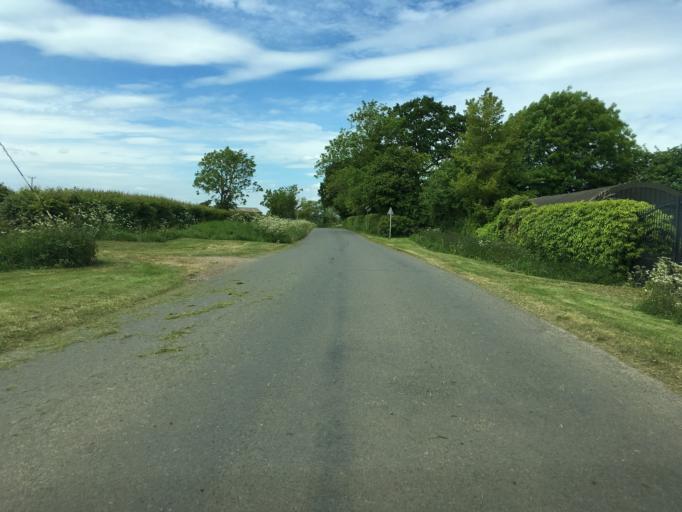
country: GB
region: England
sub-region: Gloucestershire
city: Berkeley
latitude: 51.6735
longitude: -2.4210
